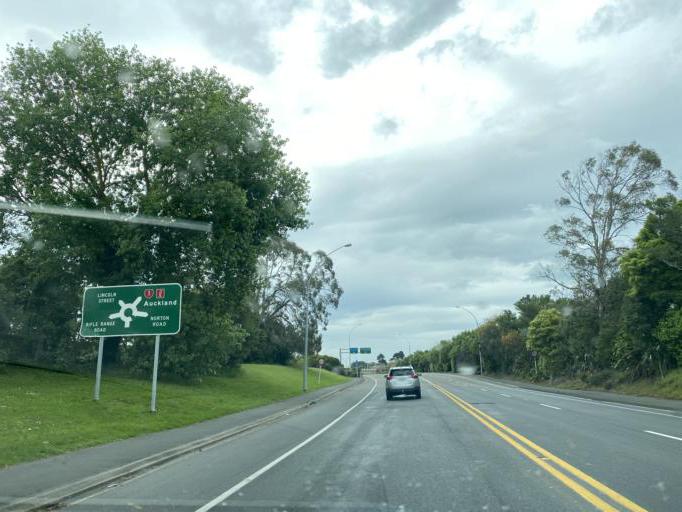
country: NZ
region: Waikato
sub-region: Hamilton City
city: Hamilton
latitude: -37.7847
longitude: 175.2548
